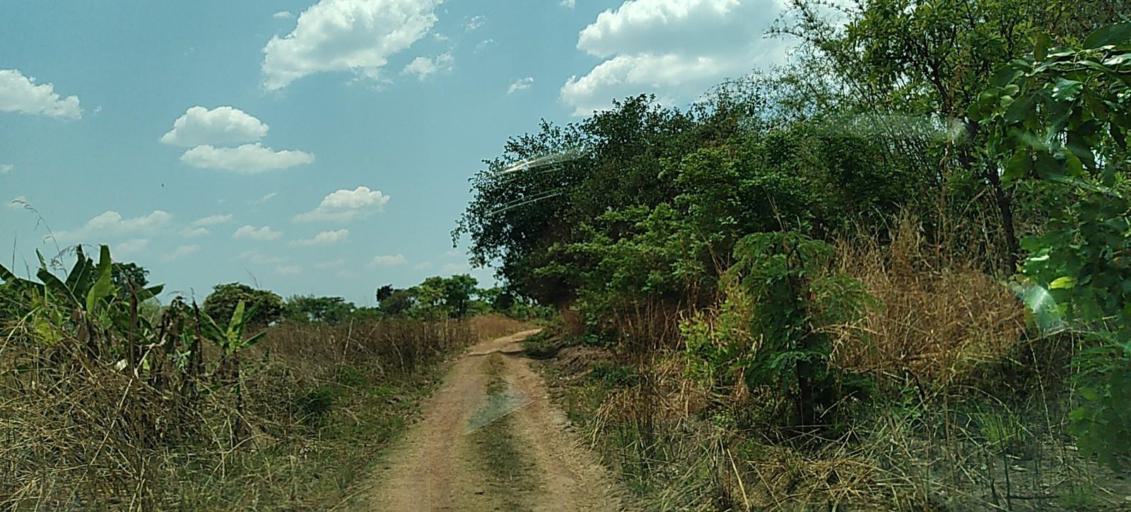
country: ZM
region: Copperbelt
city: Chililabombwe
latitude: -12.4670
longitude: 27.6666
